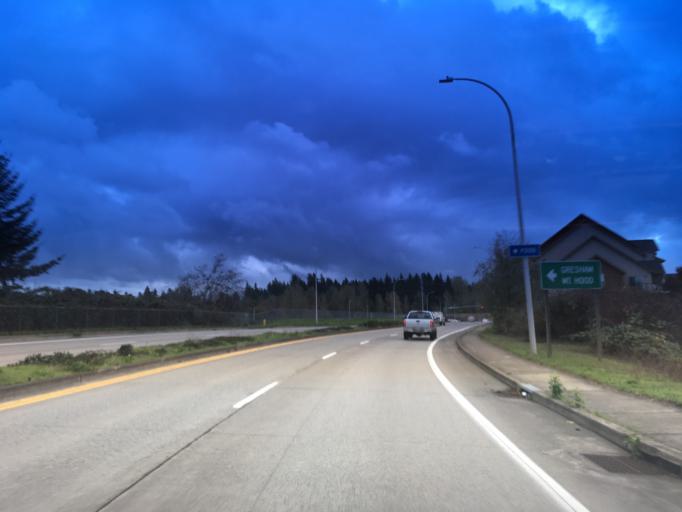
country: US
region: Oregon
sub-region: Multnomah County
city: Fairview
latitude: 45.5303
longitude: -122.4427
